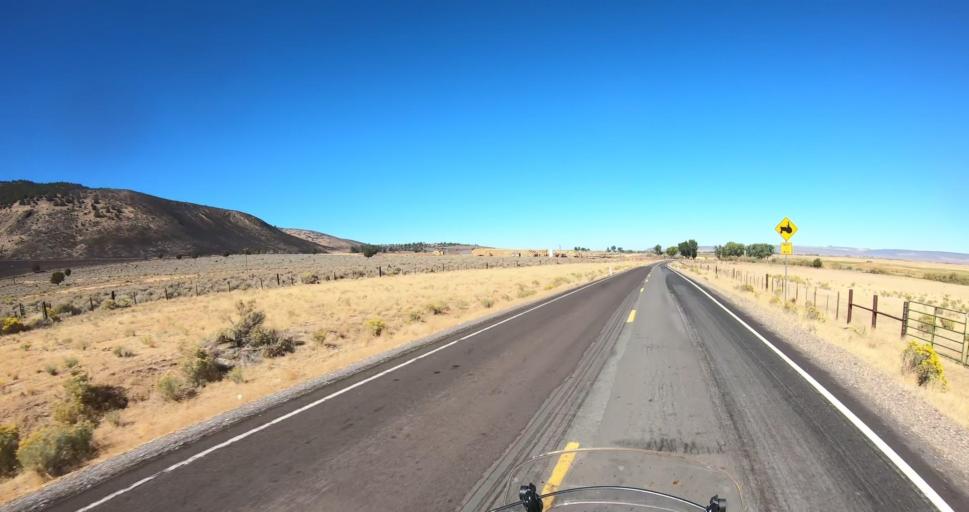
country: US
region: Oregon
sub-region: Lake County
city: Lakeview
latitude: 42.6532
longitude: -120.5228
